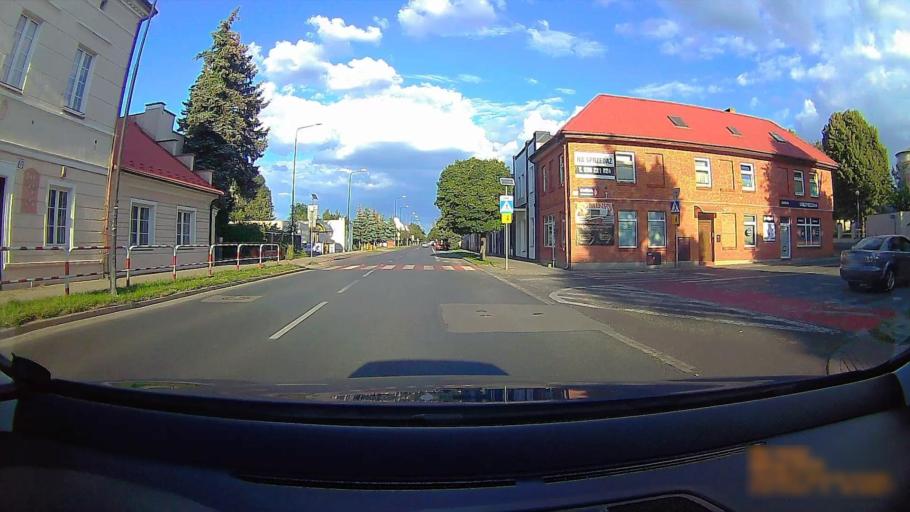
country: PL
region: Greater Poland Voivodeship
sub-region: Konin
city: Konin
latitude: 52.2045
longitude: 18.2546
